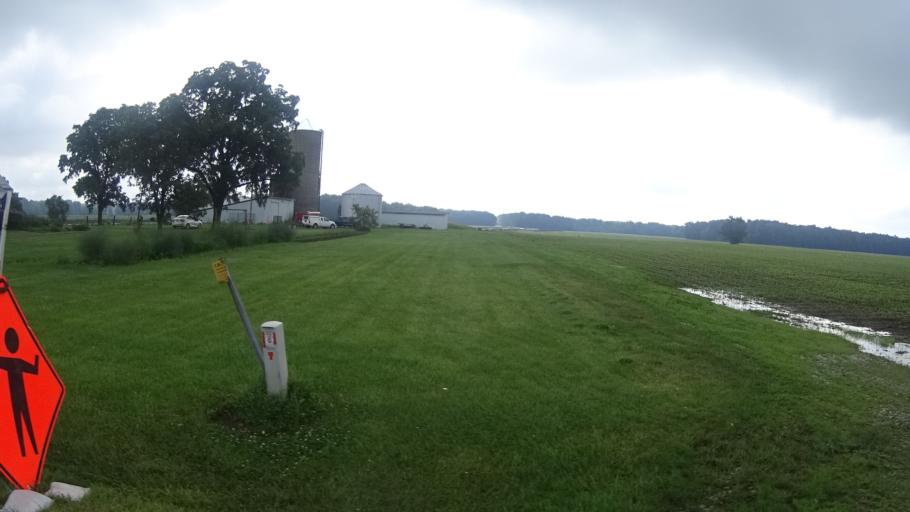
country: US
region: Ohio
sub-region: Huron County
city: Wakeman
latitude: 41.2999
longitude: -82.4429
